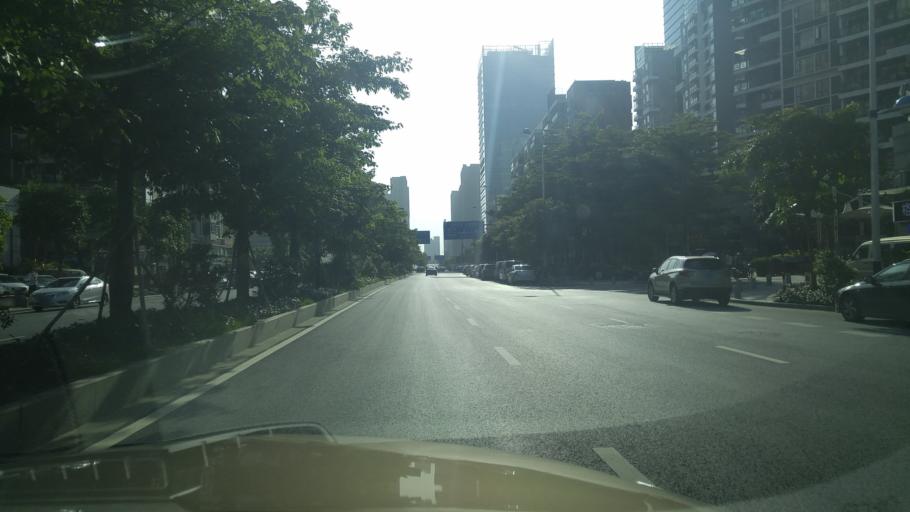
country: CN
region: Guangdong
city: Foshan
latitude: 23.0652
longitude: 113.1488
